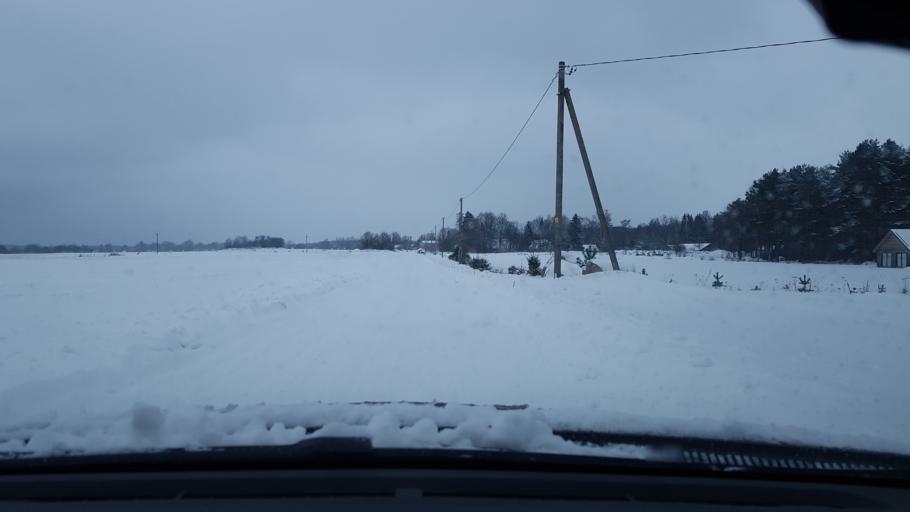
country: EE
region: Harju
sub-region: Kuusalu vald
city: Kuusalu
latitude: 59.4608
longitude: 25.4806
